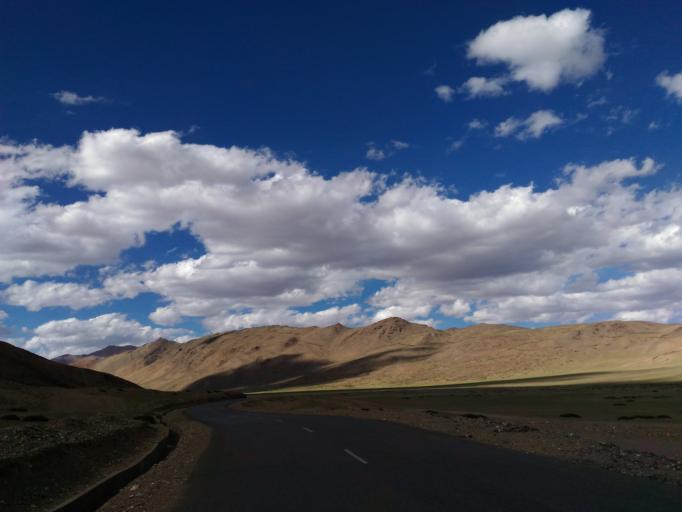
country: IN
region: Kashmir
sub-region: Ladakh
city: Leh
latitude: 33.3161
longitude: 77.9185
